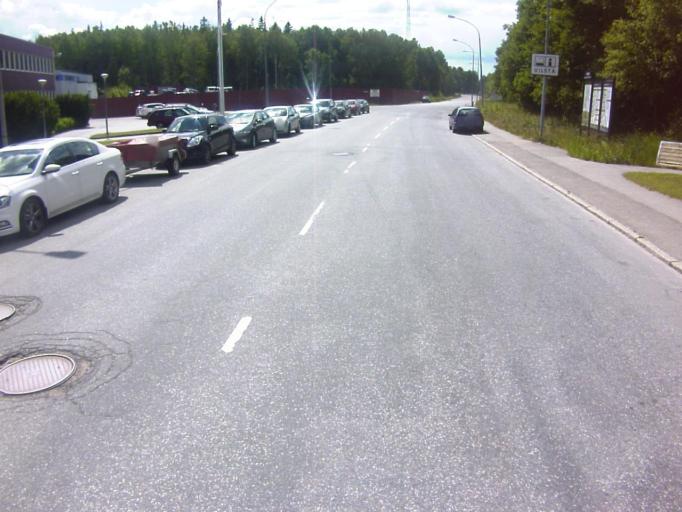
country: SE
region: Soedermanland
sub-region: Eskilstuna Kommun
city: Skogstorp
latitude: 59.3521
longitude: 16.4833
